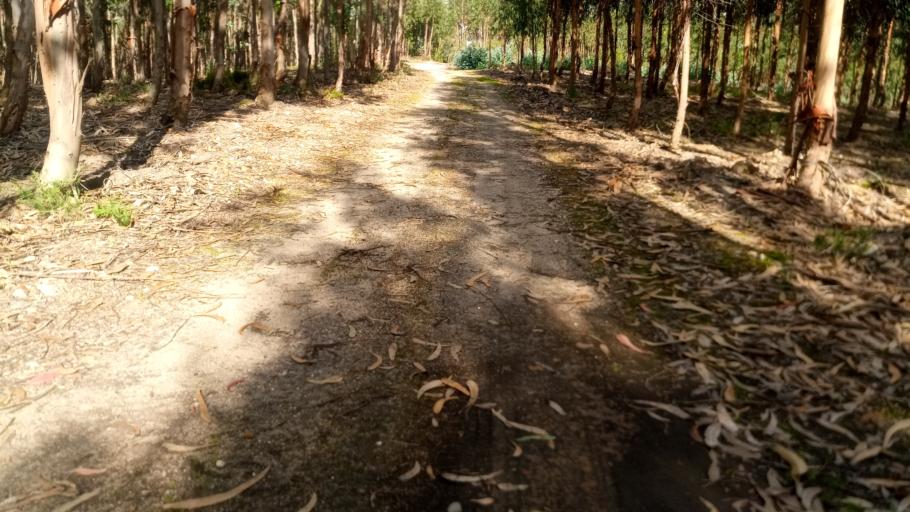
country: PT
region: Leiria
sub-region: Obidos
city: Obidos
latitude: 39.3910
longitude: -9.2037
